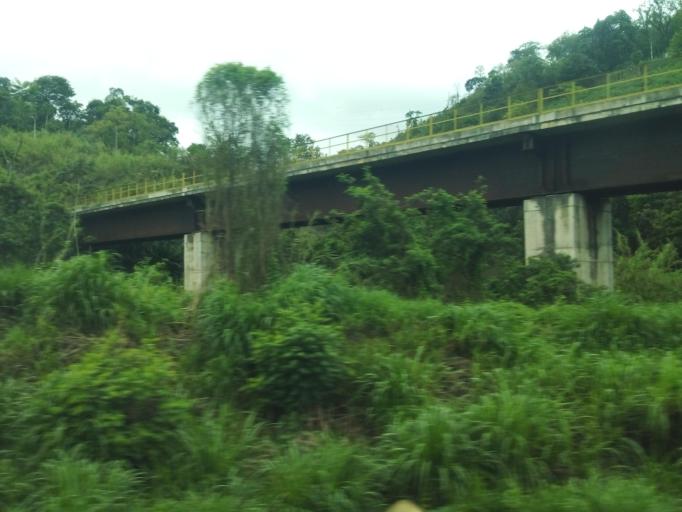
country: BR
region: Minas Gerais
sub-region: Joao Monlevade
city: Joao Monlevade
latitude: -19.8259
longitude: -43.1260
